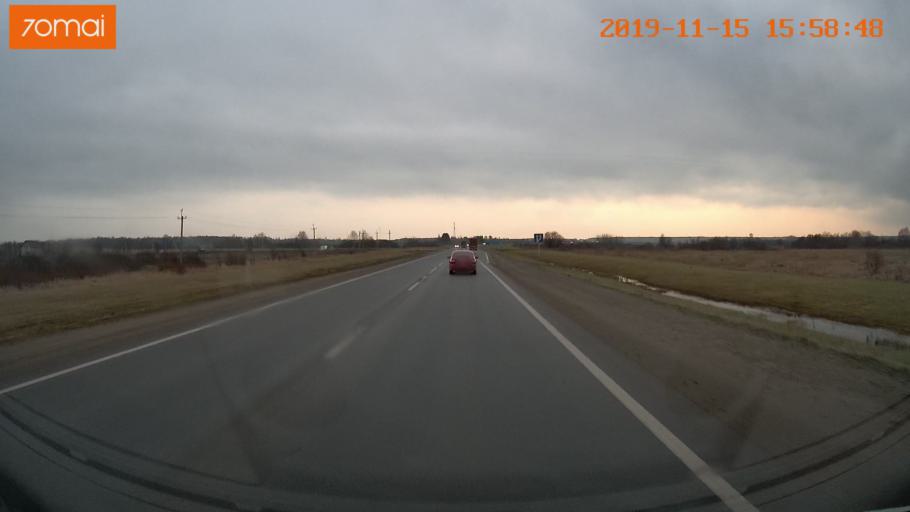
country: RU
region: Jaroslavl
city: Yaroslavl
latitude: 57.8150
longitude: 39.9524
